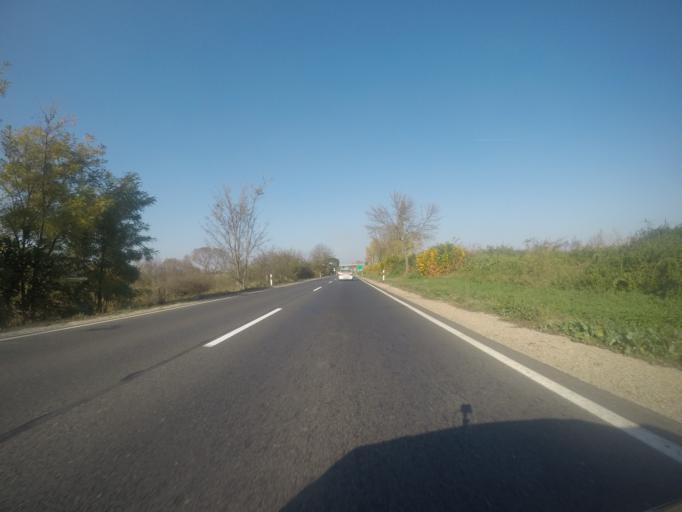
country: HU
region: Fejer
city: Baracs
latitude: 46.9055
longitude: 18.9249
